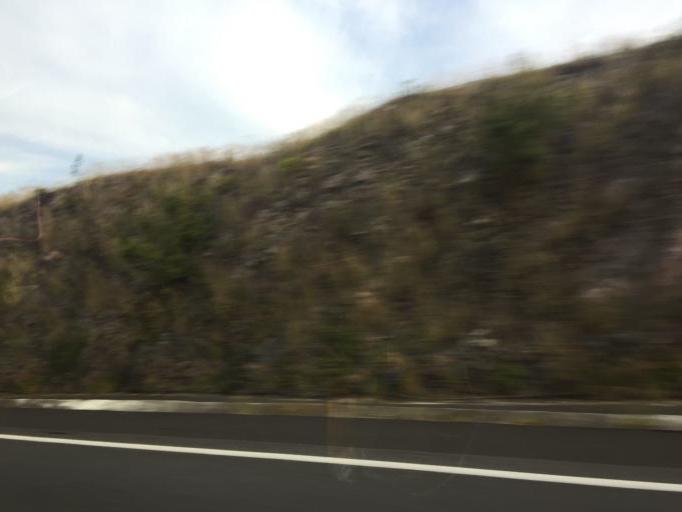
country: MX
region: Michoacan
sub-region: Zinapecuaro
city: Francisco Villa
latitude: 19.8856
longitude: -100.9184
